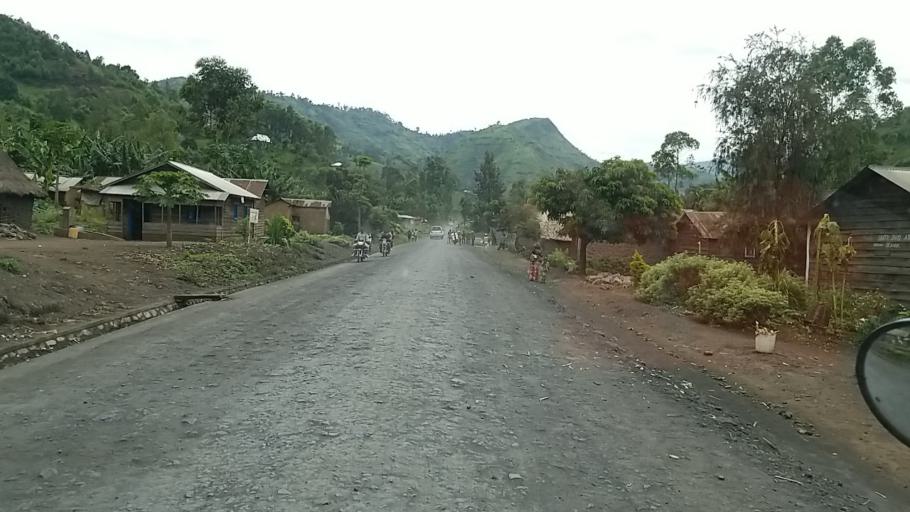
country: CD
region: Nord Kivu
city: Sake
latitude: -1.7290
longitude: 29.0090
